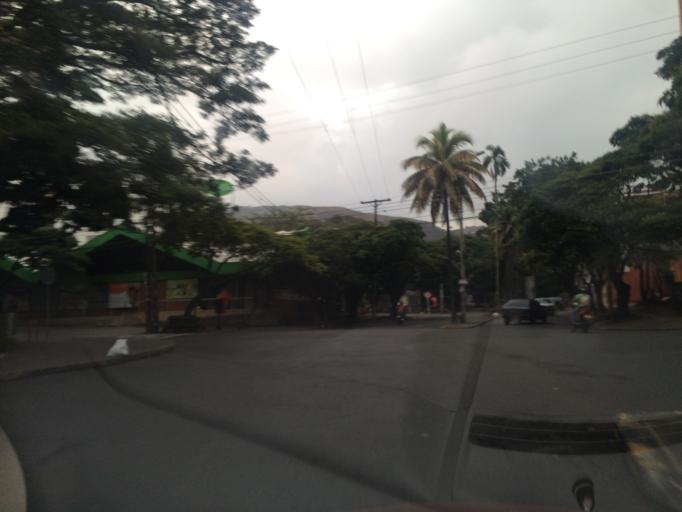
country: CO
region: Valle del Cauca
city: Cali
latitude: 3.4333
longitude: -76.5436
